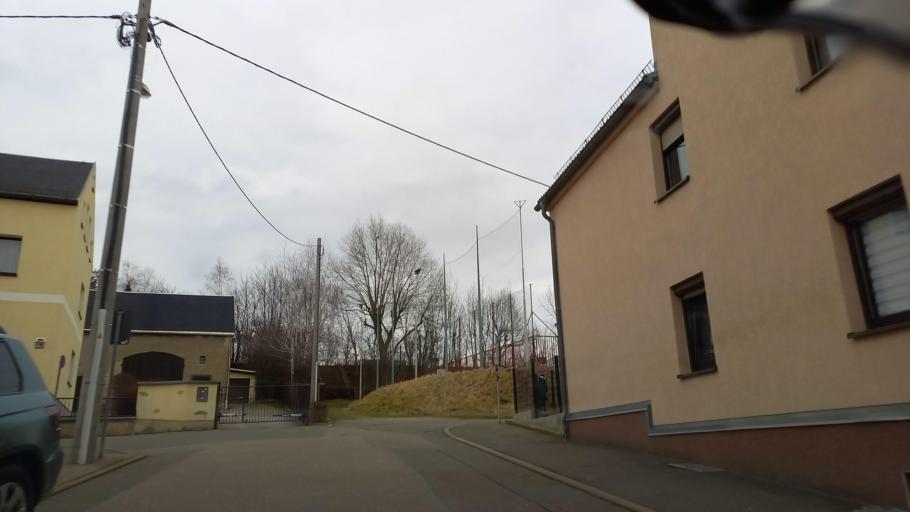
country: DE
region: Saxony
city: Wilkau-Hasslau
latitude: 50.6790
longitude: 12.5157
